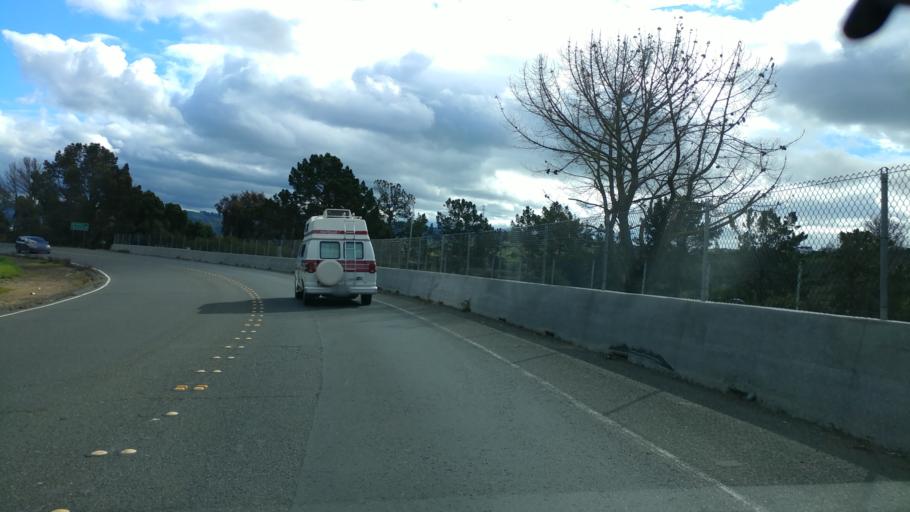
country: US
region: California
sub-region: Contra Costa County
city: Crockett
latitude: 38.0793
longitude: -122.1935
